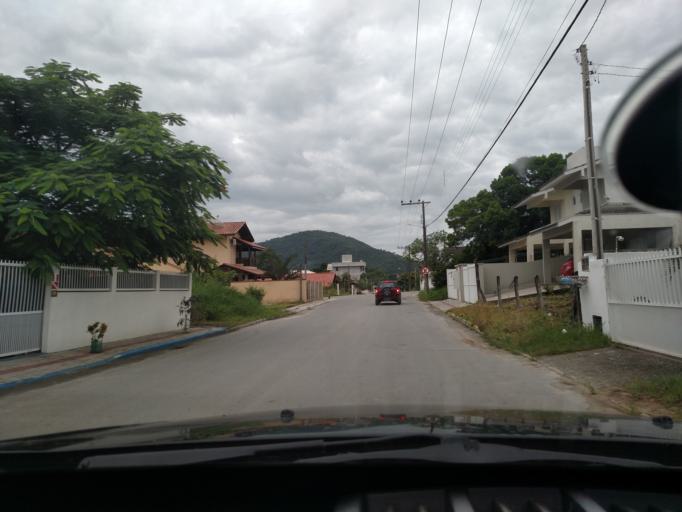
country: BR
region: Santa Catarina
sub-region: Porto Belo
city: Porto Belo
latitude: -27.1493
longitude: -48.5076
